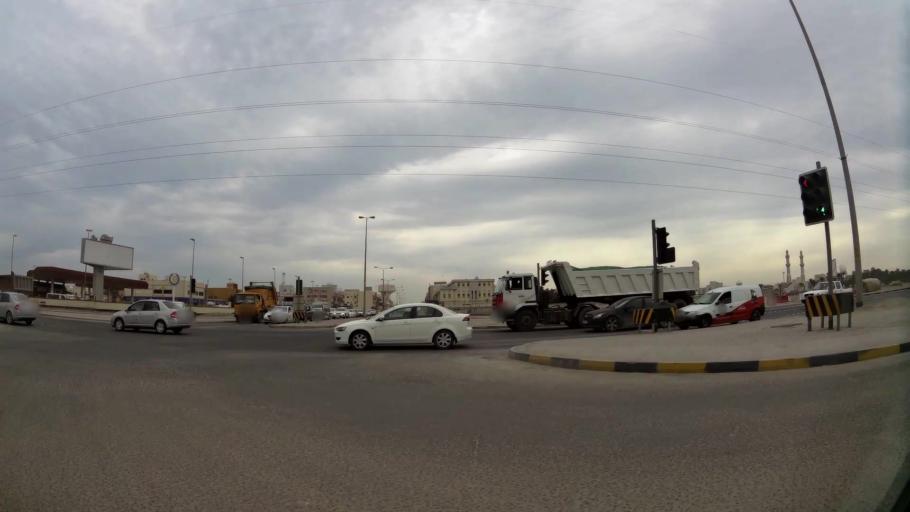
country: BH
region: Northern
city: Sitrah
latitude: 26.1646
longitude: 50.6044
